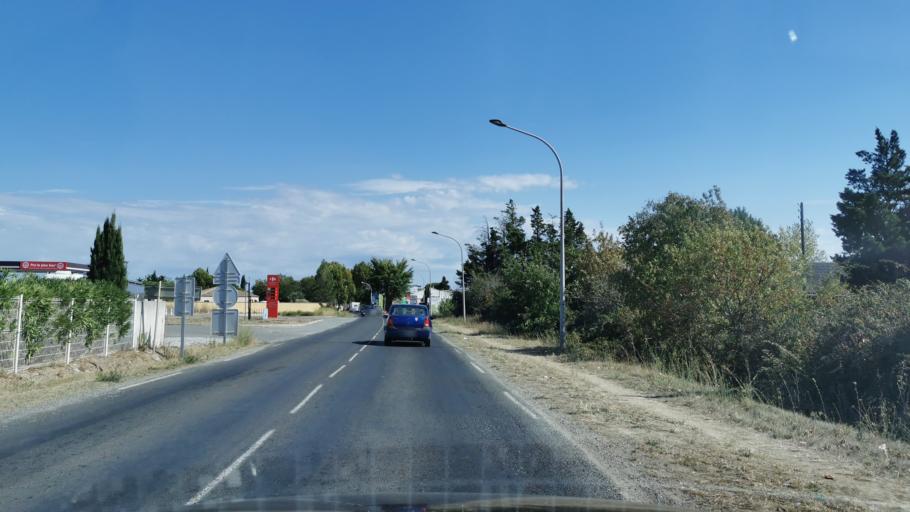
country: FR
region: Languedoc-Roussillon
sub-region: Departement de l'Aude
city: Peyriac-Minervois
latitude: 43.2849
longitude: 2.5739
